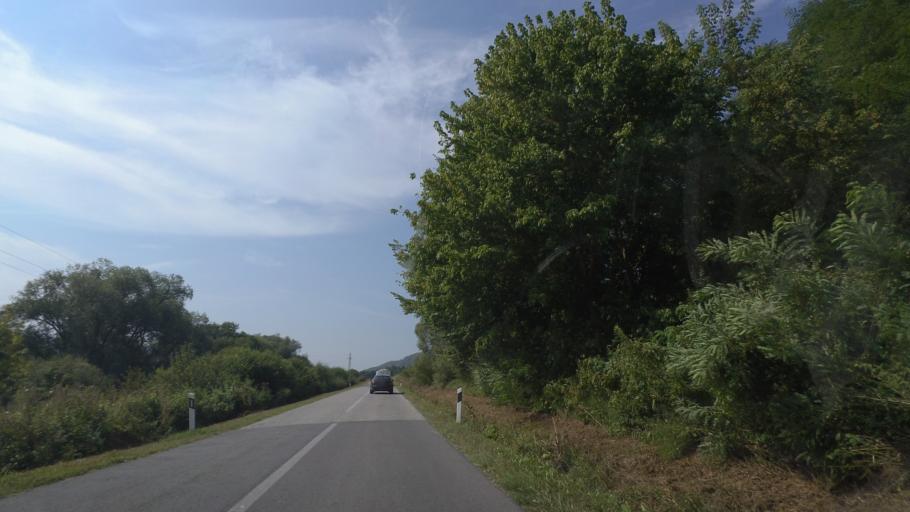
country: BA
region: Republika Srpska
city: Kostajnica
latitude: 45.2100
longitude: 16.4912
